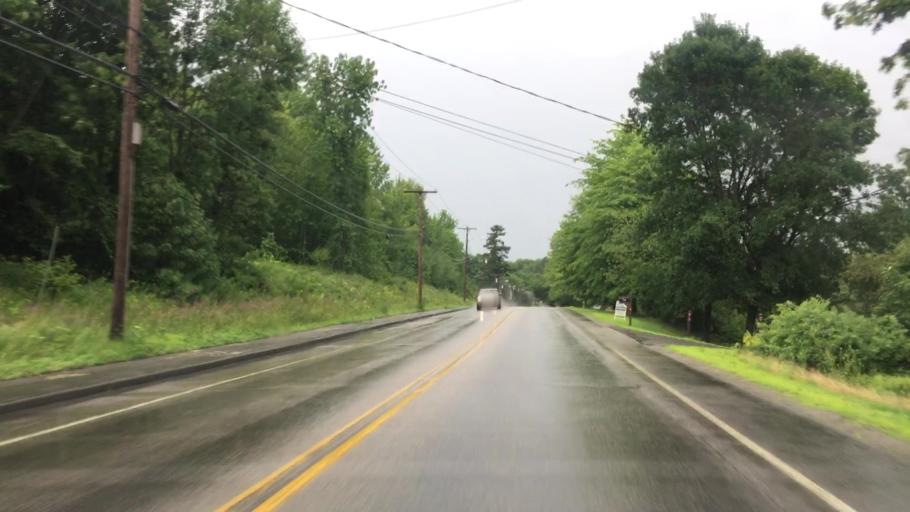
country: US
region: Maine
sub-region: Kennebec County
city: Gardiner
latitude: 44.2180
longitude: -69.7980
